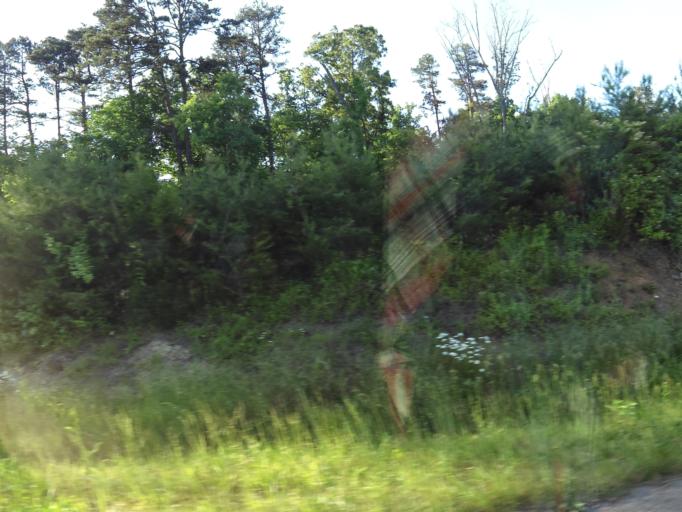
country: US
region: Tennessee
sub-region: Knox County
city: Knoxville
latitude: 35.9004
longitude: -83.8623
